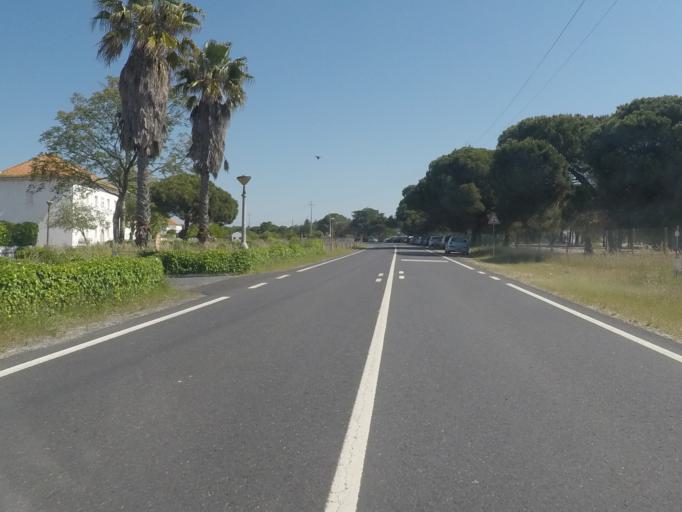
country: PT
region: Setubal
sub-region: Grandola
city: Grandola
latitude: 38.2673
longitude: -8.7279
